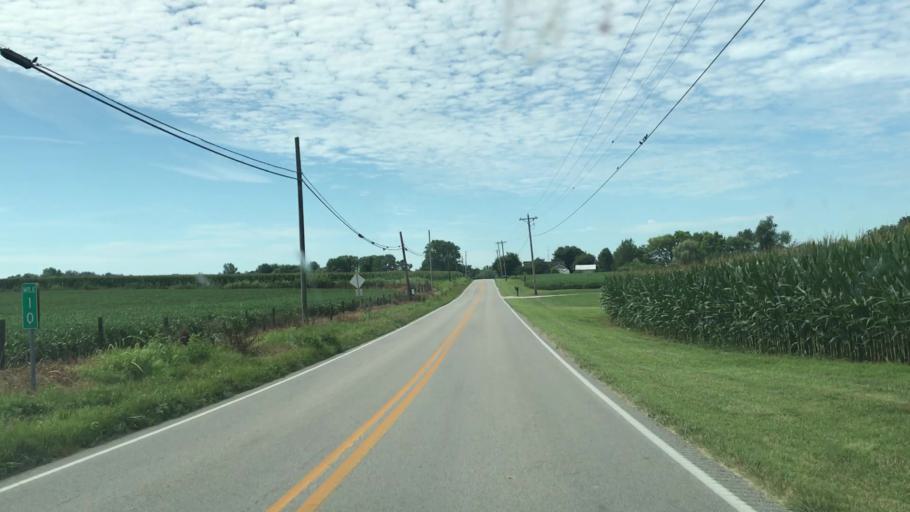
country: US
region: Kentucky
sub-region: Edmonson County
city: Brownsville
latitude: 37.0710
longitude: -86.2116
